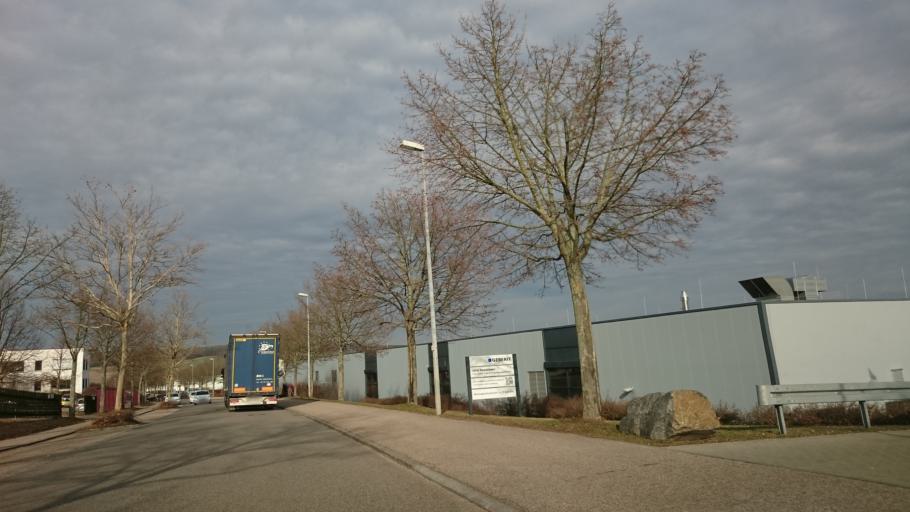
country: DE
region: Saxony
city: Sankt Egidien
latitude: 50.7775
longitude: 12.6306
